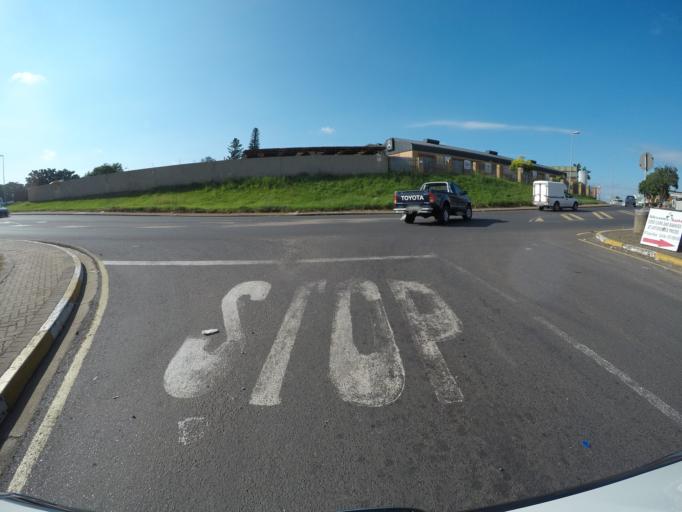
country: ZA
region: KwaZulu-Natal
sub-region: uThungulu District Municipality
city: Empangeni
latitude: -28.7660
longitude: 31.9072
